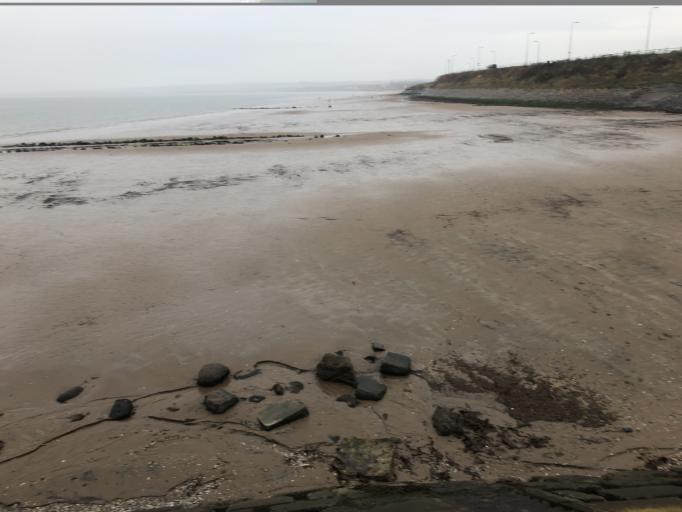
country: GB
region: Scotland
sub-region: West Lothian
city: Seafield
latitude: 55.9693
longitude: -3.1371
